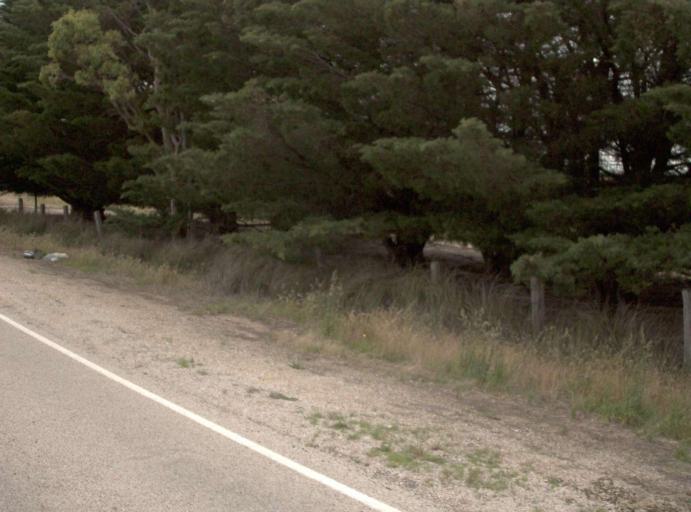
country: AU
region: Victoria
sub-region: East Gippsland
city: Bairnsdale
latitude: -37.8887
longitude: 147.5571
